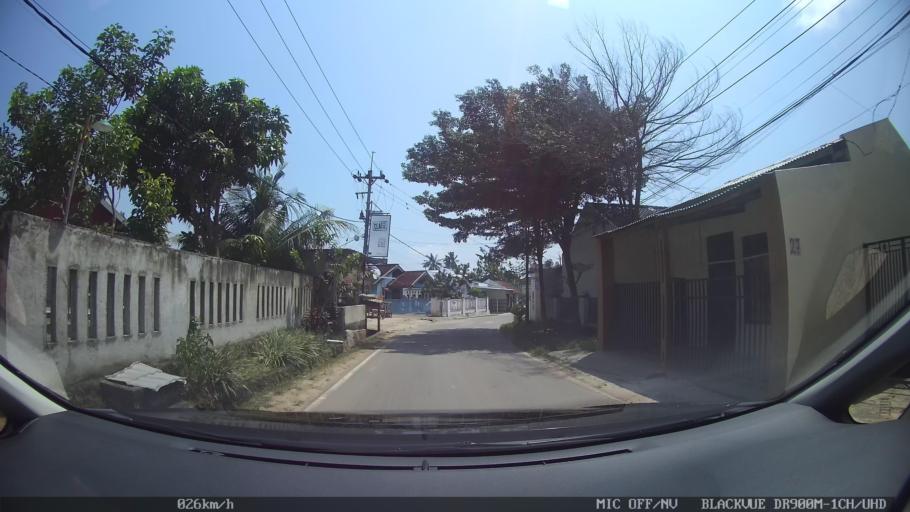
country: ID
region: Lampung
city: Kedaton
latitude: -5.3644
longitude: 105.2722
